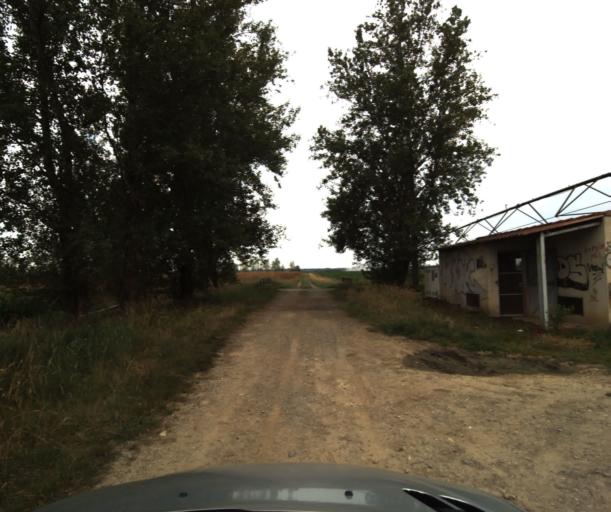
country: FR
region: Midi-Pyrenees
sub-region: Departement de la Haute-Garonne
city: Lacasse
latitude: 43.4290
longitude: 1.2658
